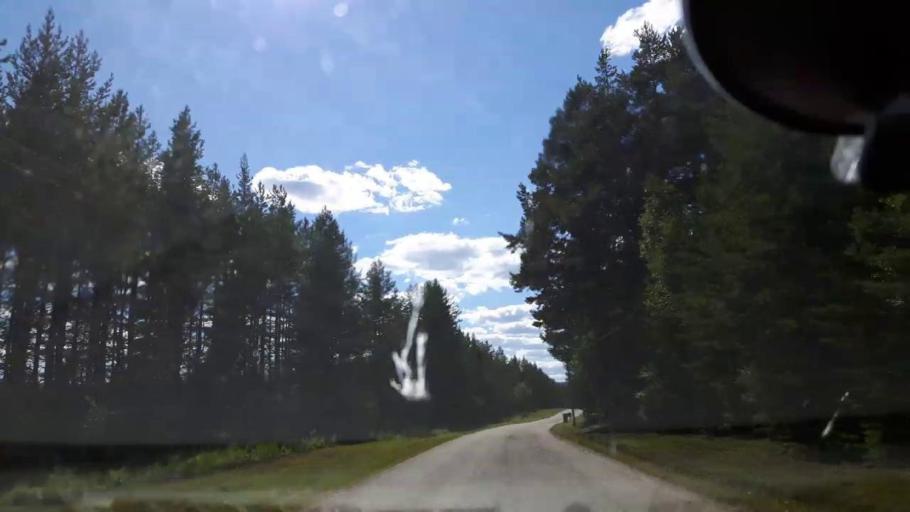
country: SE
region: Vaesternorrland
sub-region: Ange Kommun
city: Fransta
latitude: 62.7861
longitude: 16.0810
